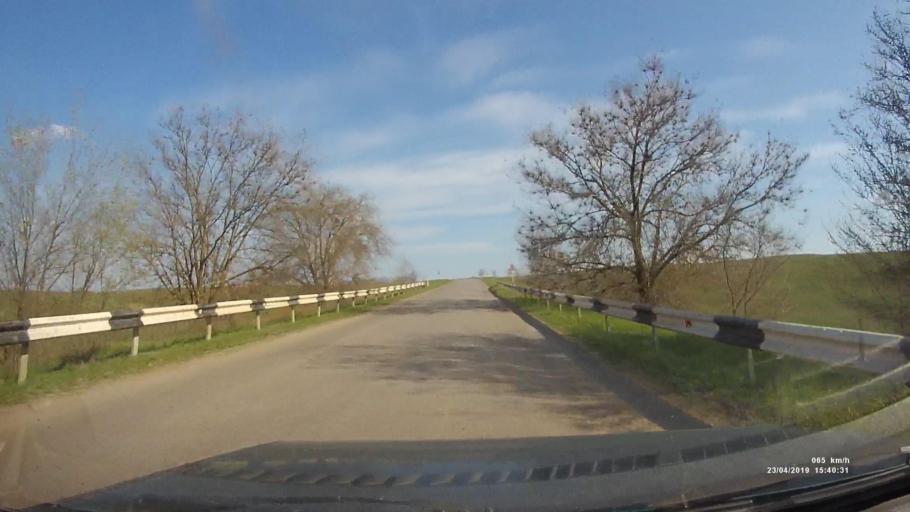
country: RU
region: Rostov
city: Remontnoye
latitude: 46.5550
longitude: 43.0392
